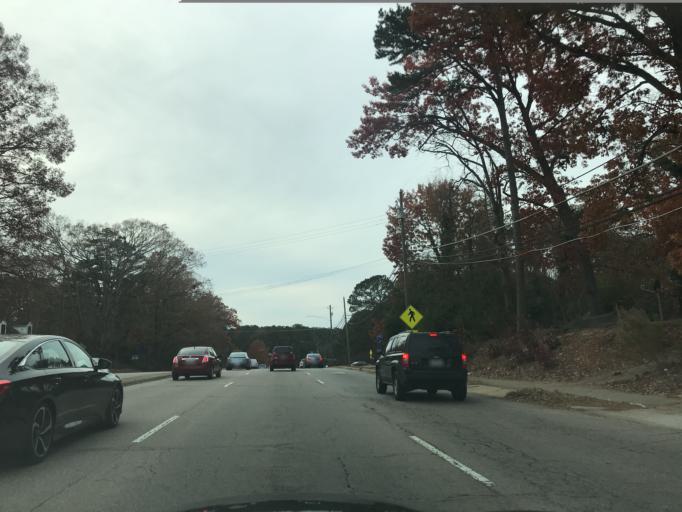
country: US
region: North Carolina
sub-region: Wake County
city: West Raleigh
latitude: 35.7840
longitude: -78.6959
